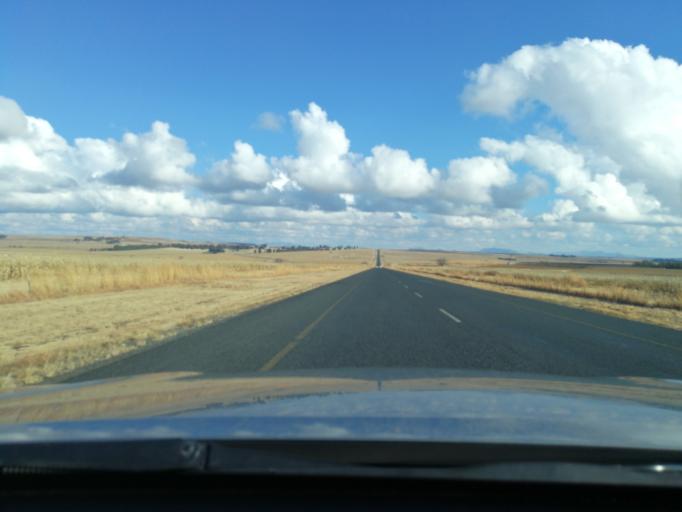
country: ZA
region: Orange Free State
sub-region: Thabo Mofutsanyana District Municipality
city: Bethlehem
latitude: -28.0902
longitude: 28.3546
